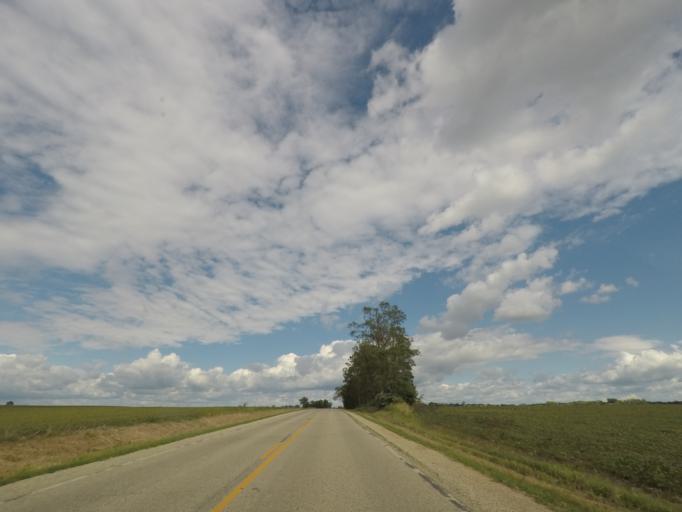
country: US
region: Wisconsin
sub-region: Rock County
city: Orfordville
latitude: 42.7052
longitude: -89.1613
